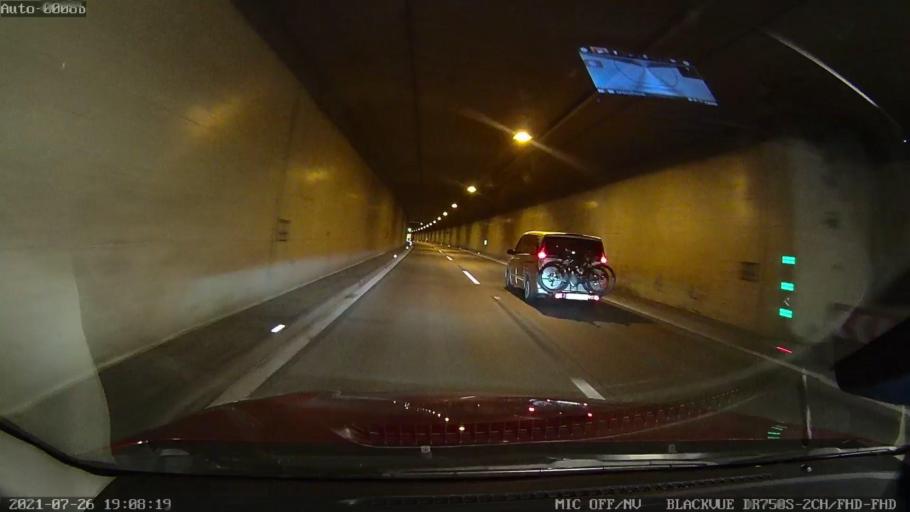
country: AT
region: Upper Austria
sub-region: Wels-Land
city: Steinhaus
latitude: 48.1125
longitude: 14.0124
